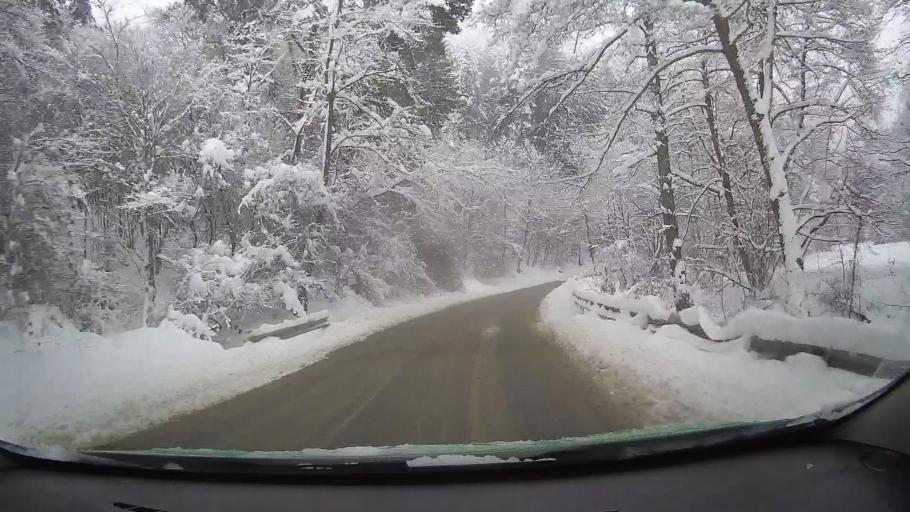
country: RO
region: Sibiu
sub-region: Comuna Tilisca
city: Tilisca
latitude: 45.8043
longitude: 23.8149
